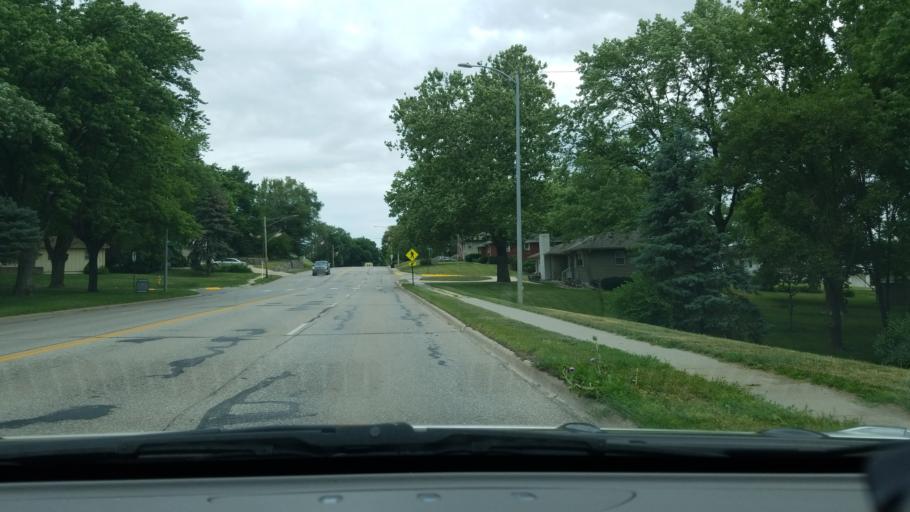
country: US
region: Nebraska
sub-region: Sarpy County
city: Papillion
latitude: 41.1465
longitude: -96.0429
